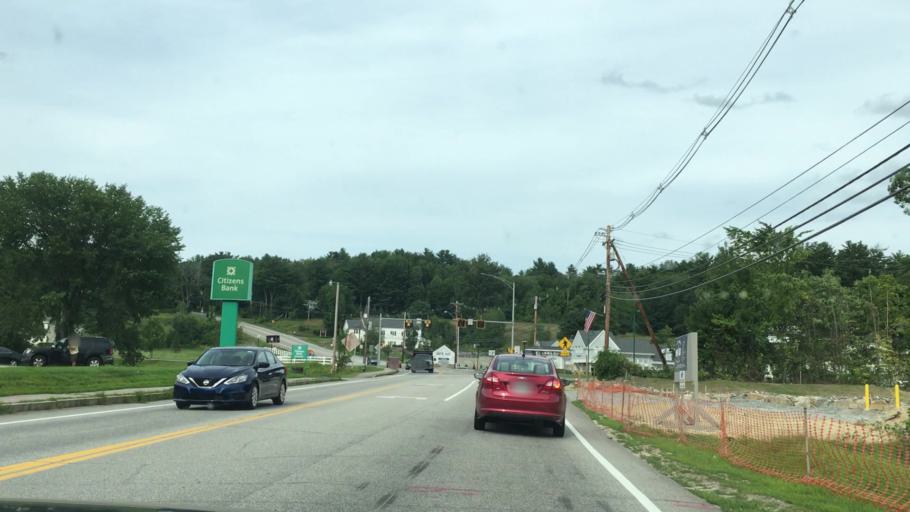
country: US
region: New Hampshire
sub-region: Belknap County
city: Meredith
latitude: 43.6613
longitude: -71.4950
